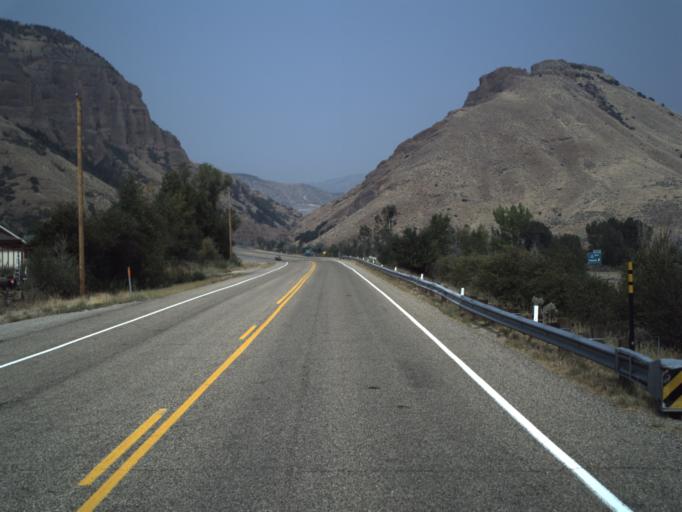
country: US
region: Utah
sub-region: Morgan County
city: Morgan
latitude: 41.0395
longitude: -111.5182
